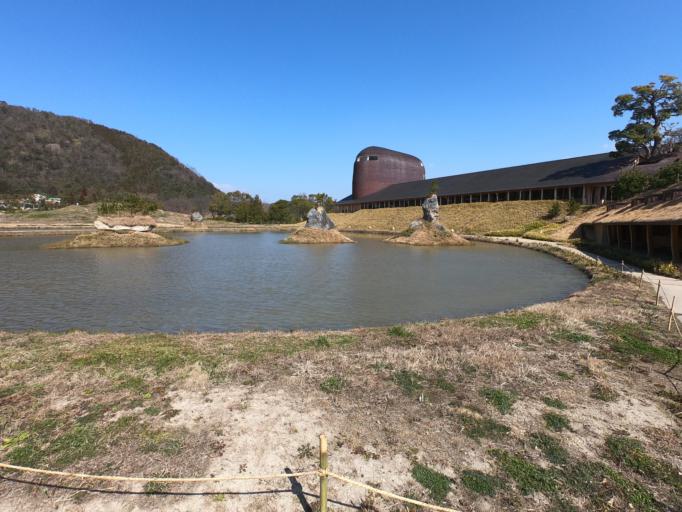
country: JP
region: Shiga Prefecture
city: Omihachiman
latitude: 35.1495
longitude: 136.0606
